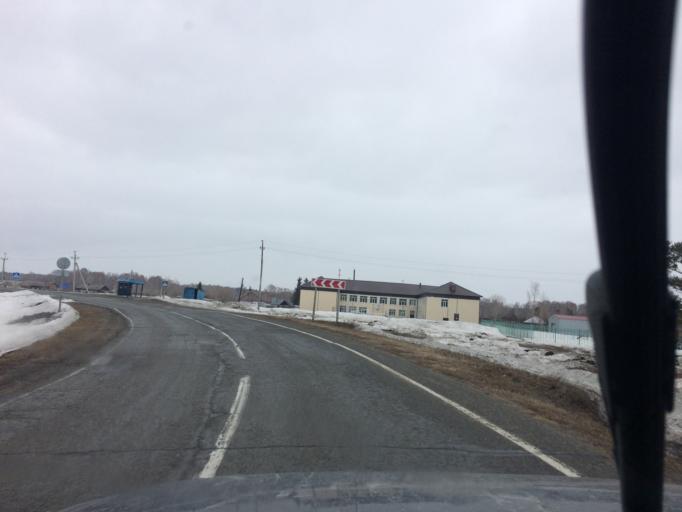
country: RU
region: Novosibirsk
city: Tashara
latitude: 55.4727
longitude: 83.4483
